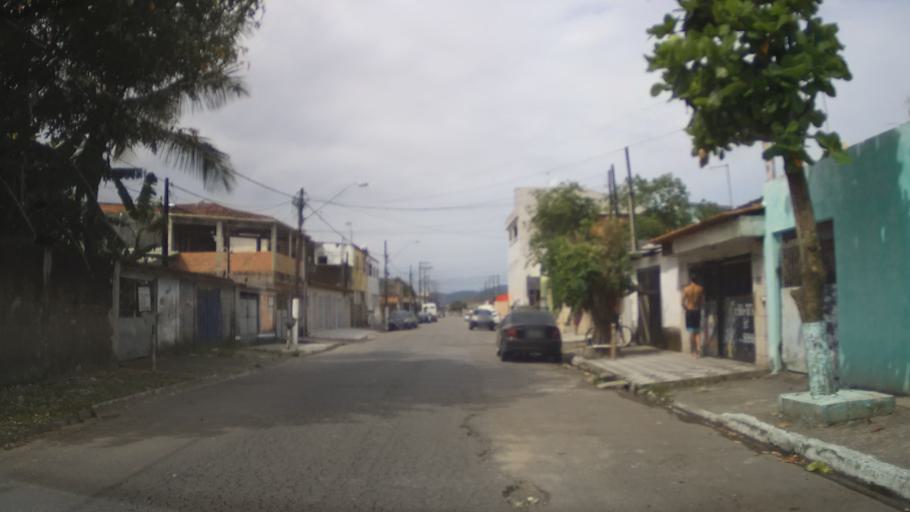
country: BR
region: Sao Paulo
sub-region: Praia Grande
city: Praia Grande
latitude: -24.0017
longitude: -46.4502
